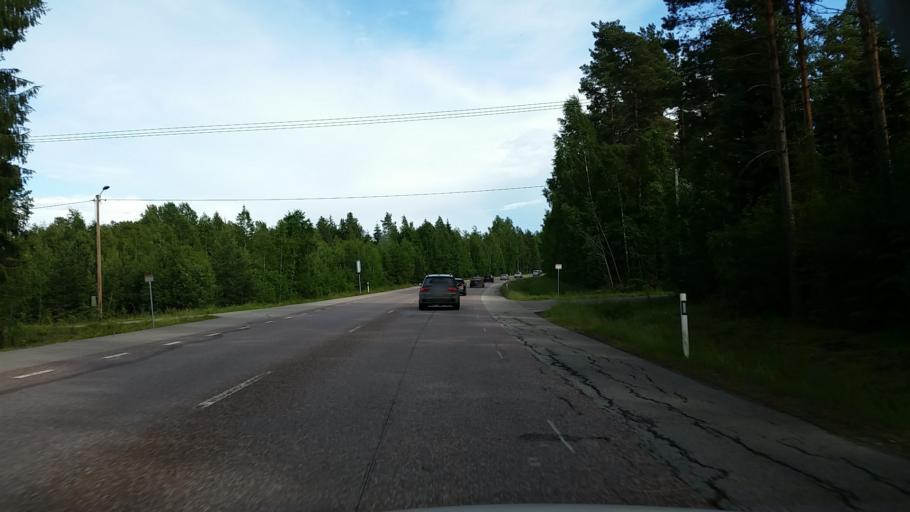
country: SE
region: Dalarna
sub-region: Smedjebackens Kommun
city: Smedjebacken
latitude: 60.0937
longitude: 15.5252
